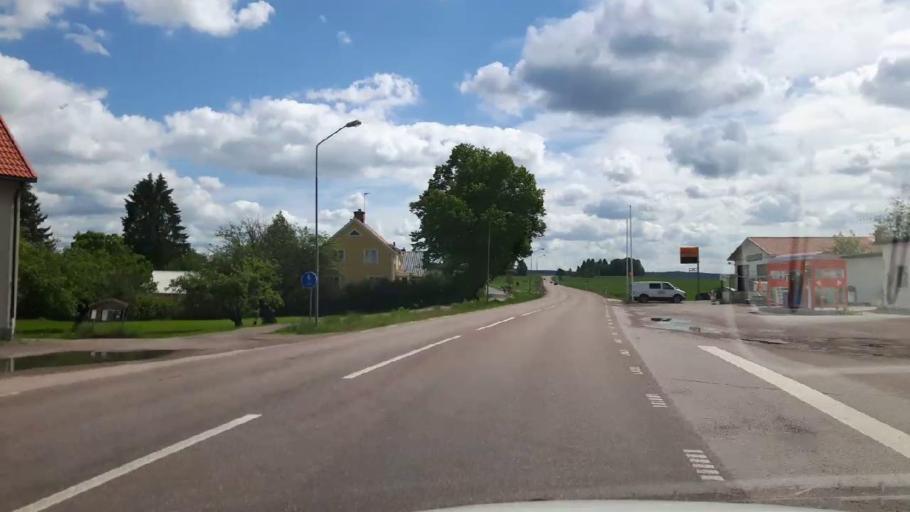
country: SE
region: Dalarna
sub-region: Hedemora Kommun
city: Langshyttan
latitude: 60.3958
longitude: 15.8886
